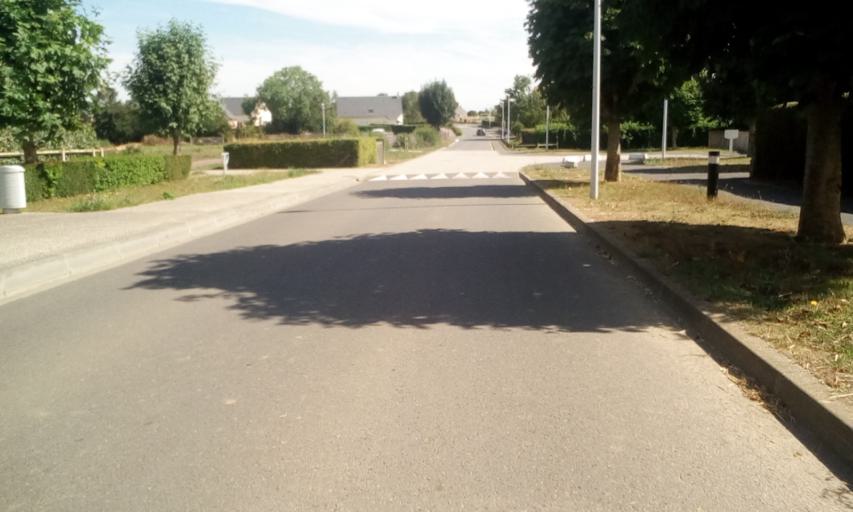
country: FR
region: Lower Normandy
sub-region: Departement du Calvados
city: Eterville
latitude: 49.1478
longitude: -0.4245
